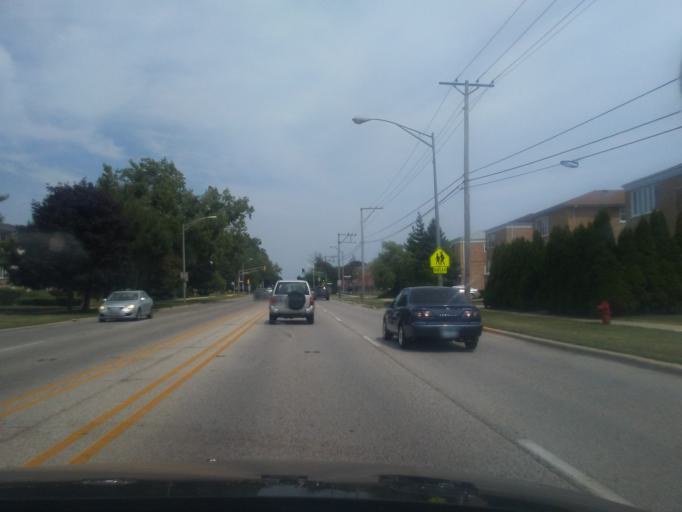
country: US
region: Illinois
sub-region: Cook County
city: Norridge
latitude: 41.9666
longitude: -87.8331
